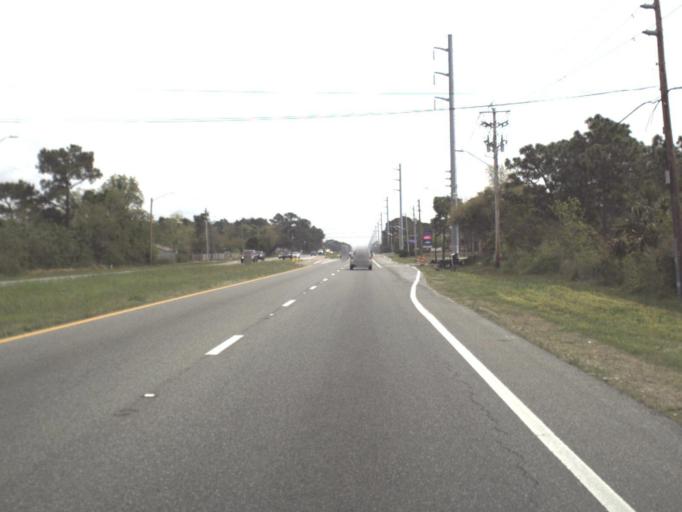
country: US
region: Florida
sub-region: Santa Rosa County
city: Oriole Beach
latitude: 30.3881
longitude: -87.0776
